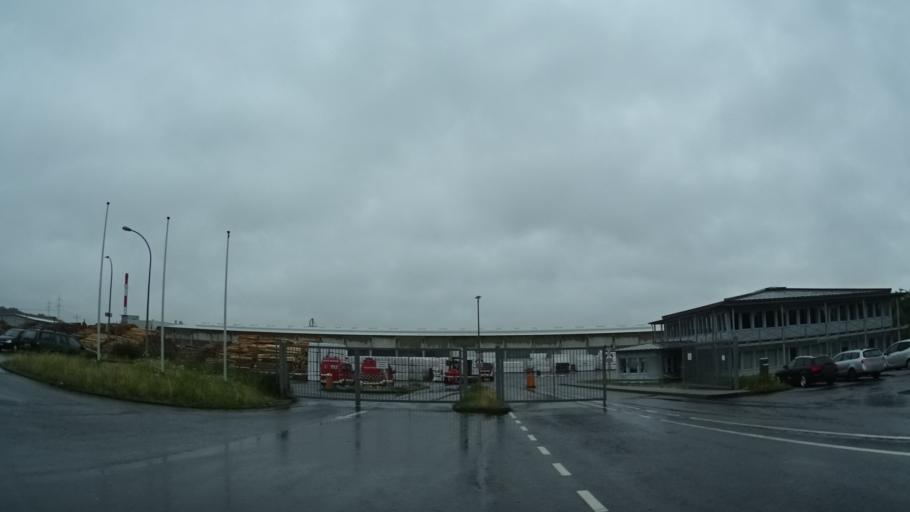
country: DE
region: Rheinland-Pfalz
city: Steinwenden
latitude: 49.4350
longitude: 7.5213
